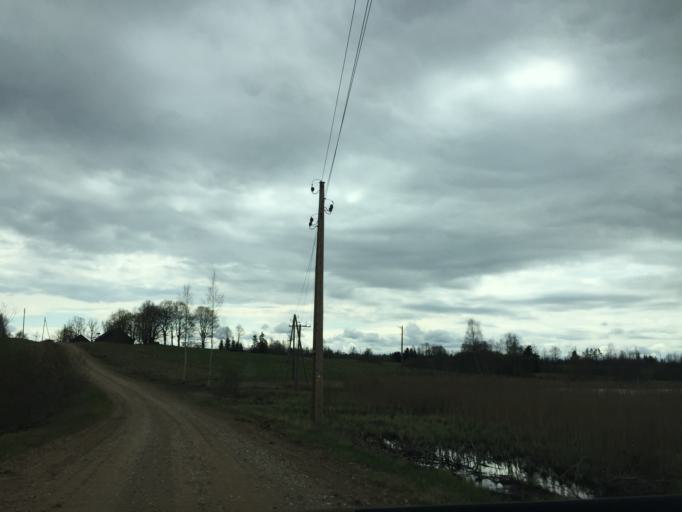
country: LV
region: Jaunpiebalga
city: Jaunpiebalga
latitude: 57.1446
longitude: 25.9292
